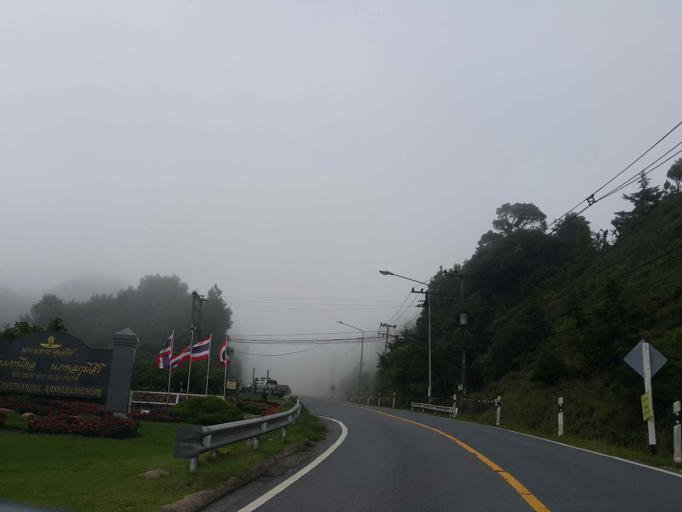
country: TH
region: Chiang Mai
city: Mae Chaem
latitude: 18.5513
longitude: 98.4815
